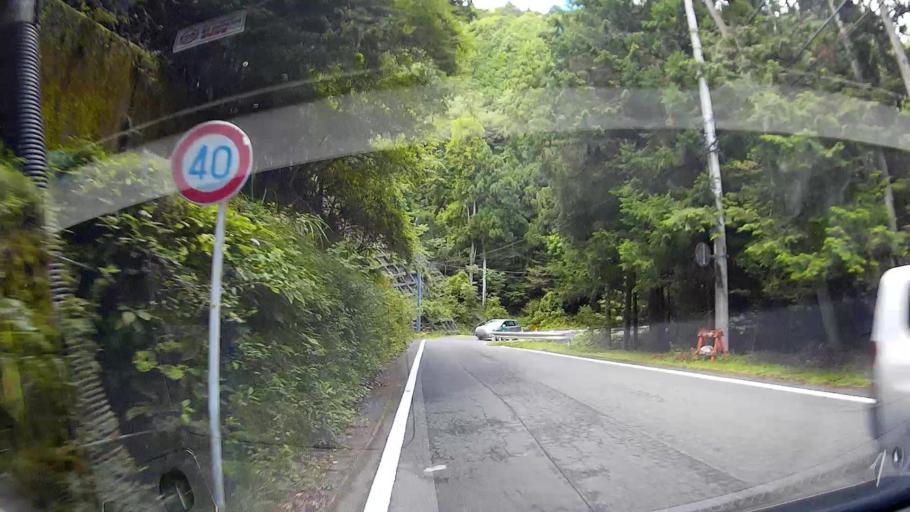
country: JP
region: Shizuoka
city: Shizuoka-shi
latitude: 35.2295
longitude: 138.2479
